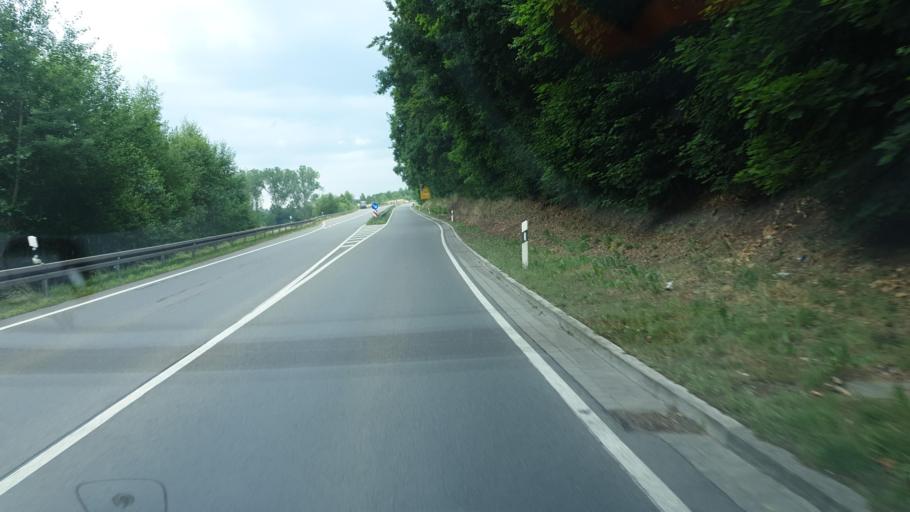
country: DE
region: Saxony
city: Reichenbach/Vogtland
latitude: 50.6134
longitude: 12.3139
